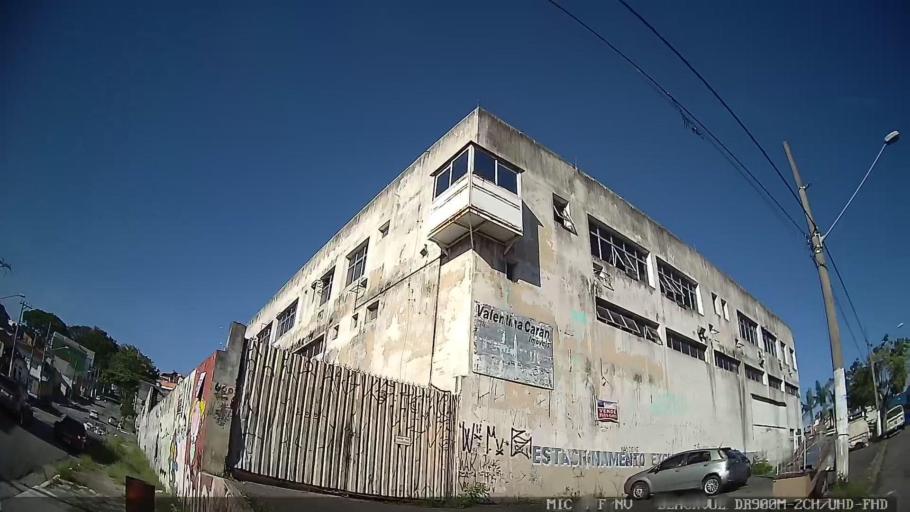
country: BR
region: Sao Paulo
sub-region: Sao Caetano Do Sul
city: Sao Caetano do Sul
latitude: -23.5498
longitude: -46.5229
